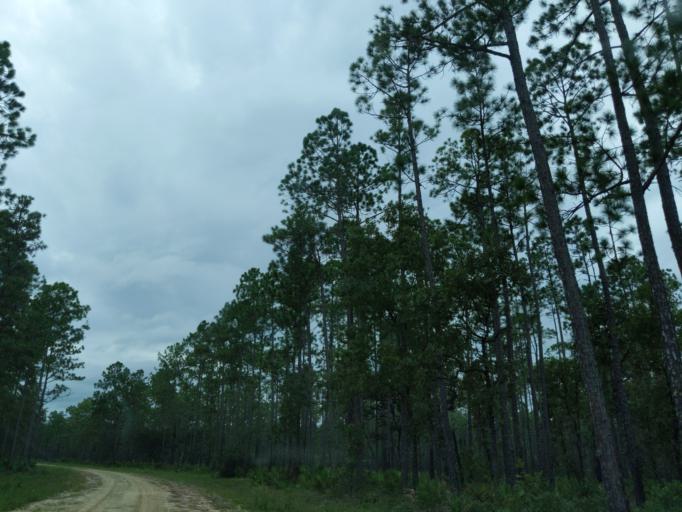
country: US
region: Florida
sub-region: Gadsden County
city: Midway
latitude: 30.3511
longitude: -84.5084
